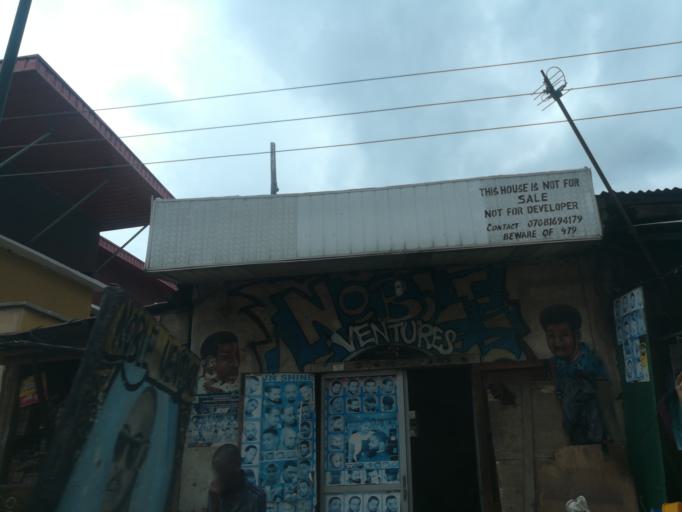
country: NG
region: Lagos
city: Ikeja
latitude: 6.5956
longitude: 3.3430
